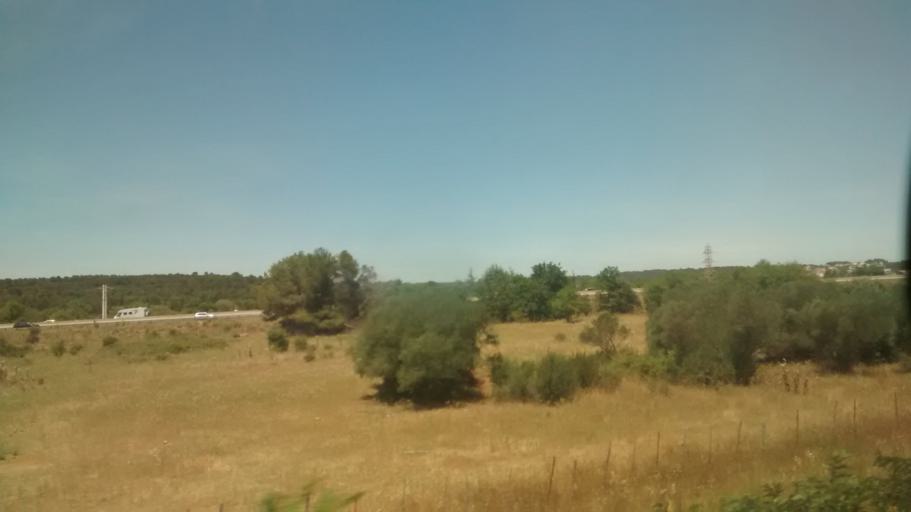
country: FR
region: Languedoc-Roussillon
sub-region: Departement du Gard
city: Milhaud
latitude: 43.7998
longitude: 4.3143
